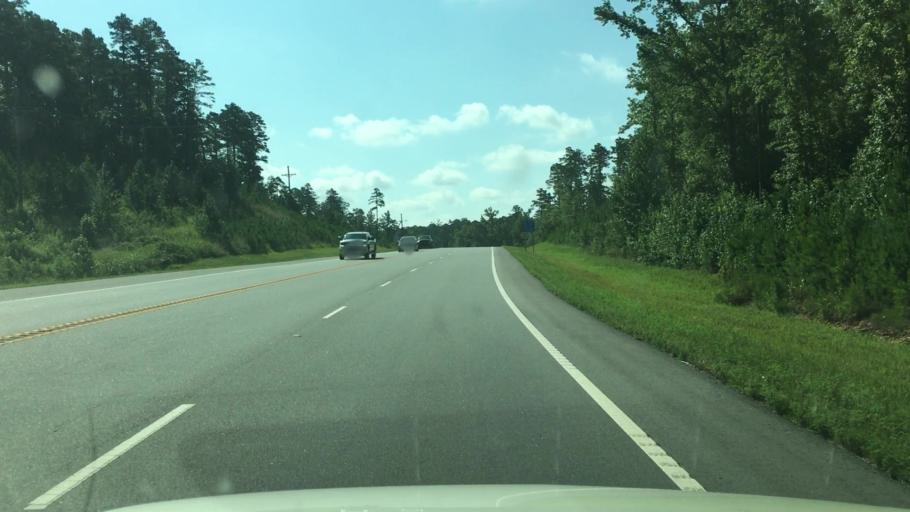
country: US
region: Arkansas
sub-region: Garland County
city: Piney
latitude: 34.5214
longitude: -93.3171
